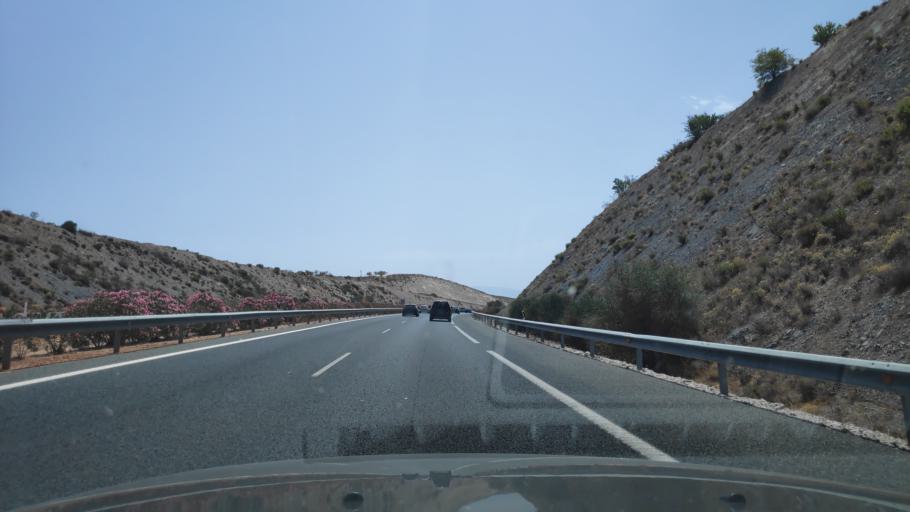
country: ES
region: Andalusia
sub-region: Provincia de Granada
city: Padul
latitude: 37.0030
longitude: -3.6341
